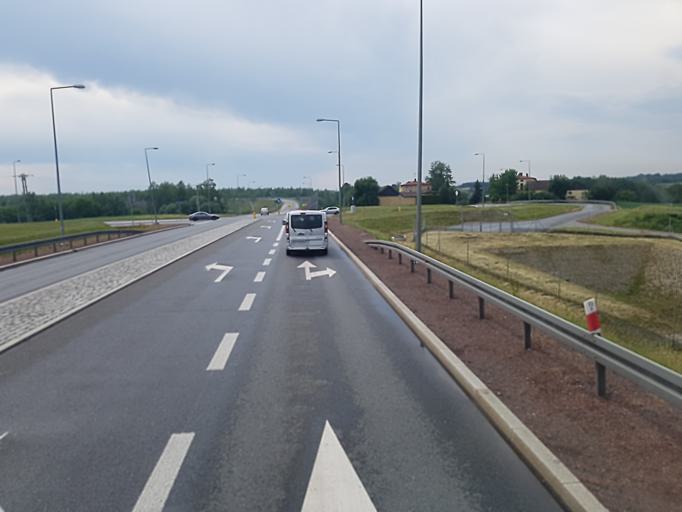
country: PL
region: Silesian Voivodeship
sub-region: Jastrzebie-Zdroj
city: Jastrzebie Zdroj
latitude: 49.9725
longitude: 18.5684
